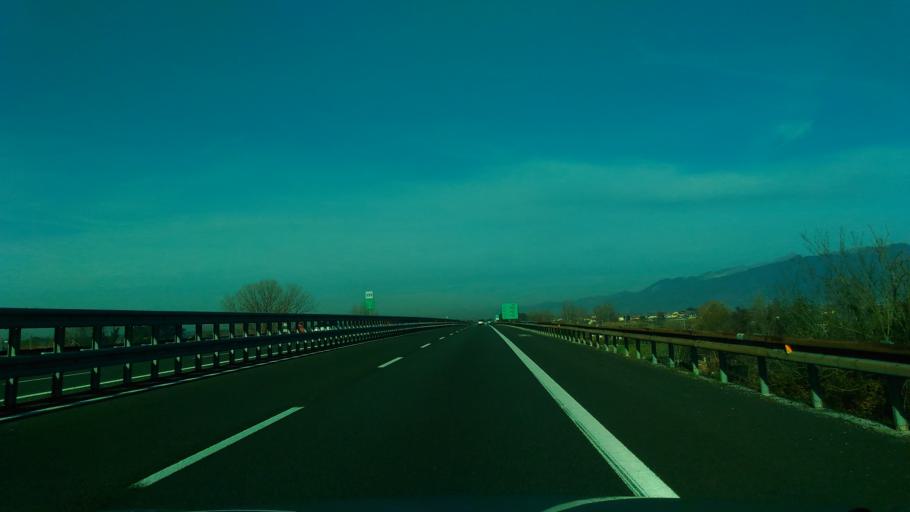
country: IT
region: Tuscany
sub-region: Provincia di Lucca
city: Camaiore
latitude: 43.9003
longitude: 10.2514
